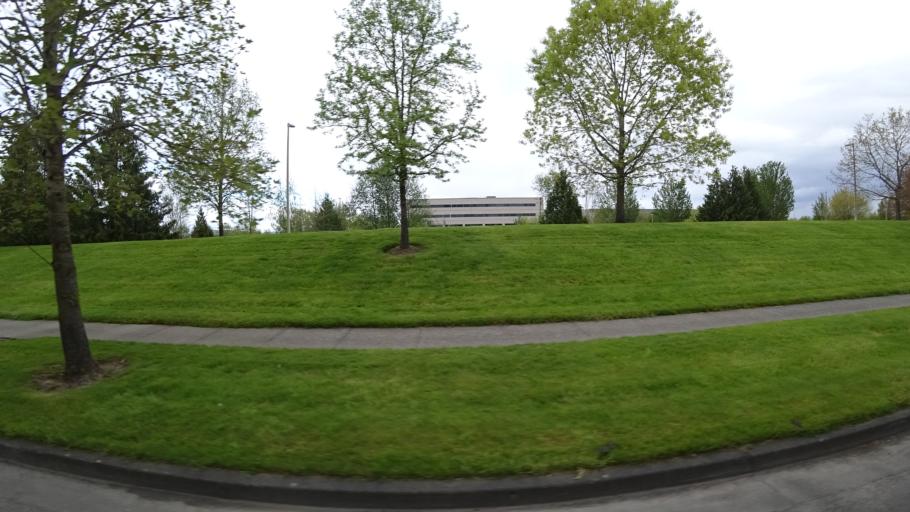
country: US
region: Oregon
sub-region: Washington County
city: Hillsboro
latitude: 45.5434
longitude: -122.9664
